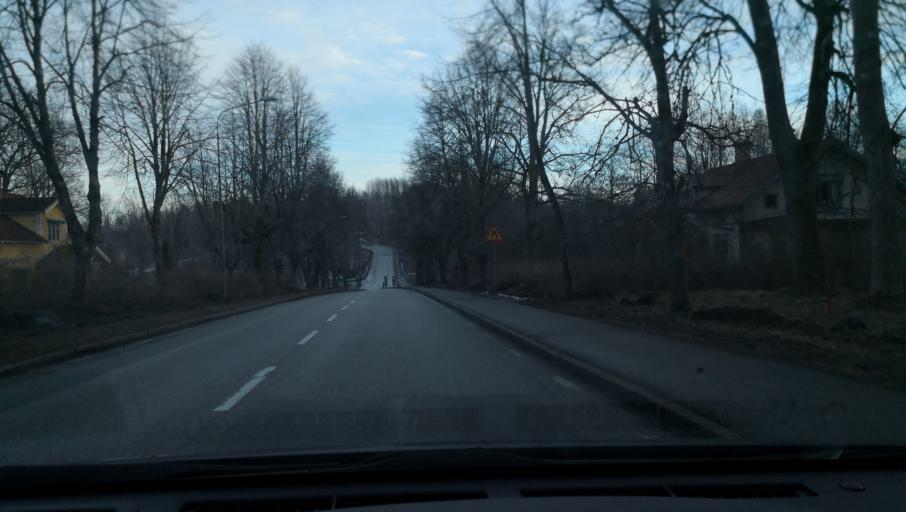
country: SE
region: OErebro
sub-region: Degerfors Kommun
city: Degerfors
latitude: 59.1248
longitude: 14.5213
